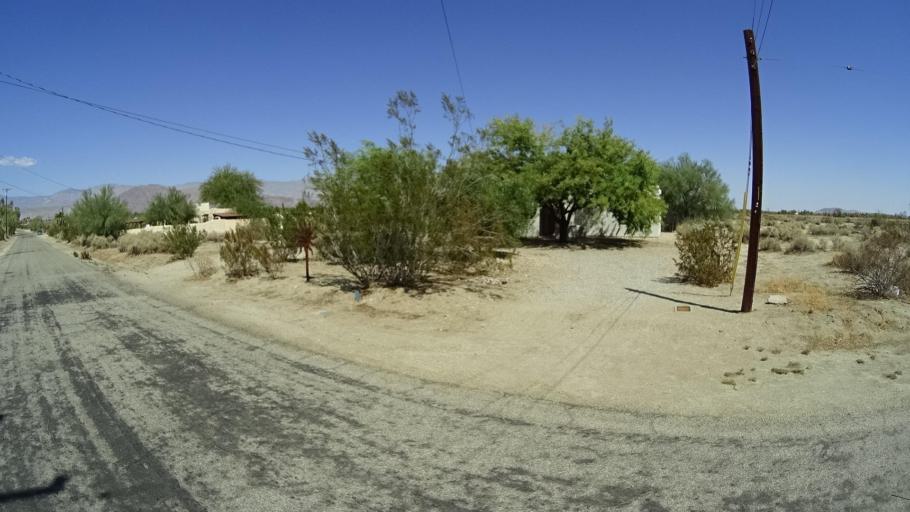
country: US
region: California
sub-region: San Diego County
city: Borrego Springs
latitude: 33.2448
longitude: -116.3710
